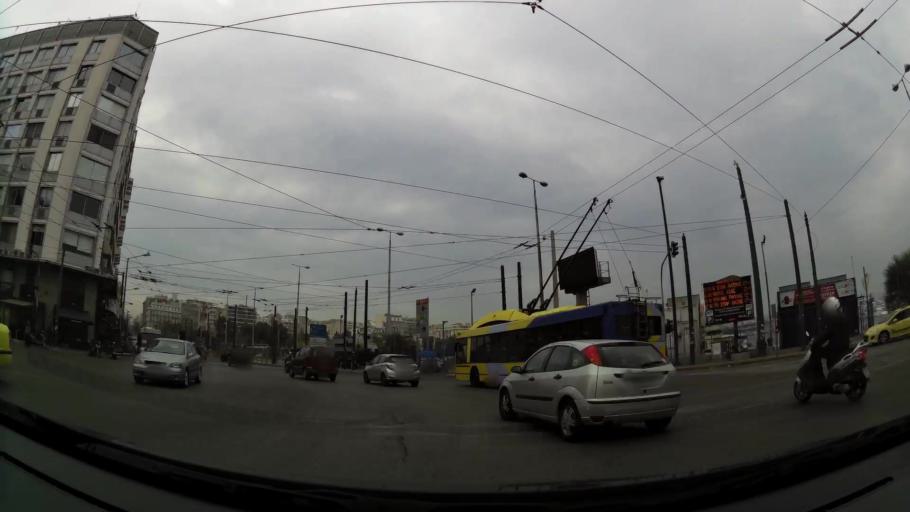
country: GR
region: Attica
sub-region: Nomos Attikis
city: Piraeus
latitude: 37.9456
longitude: 23.6423
